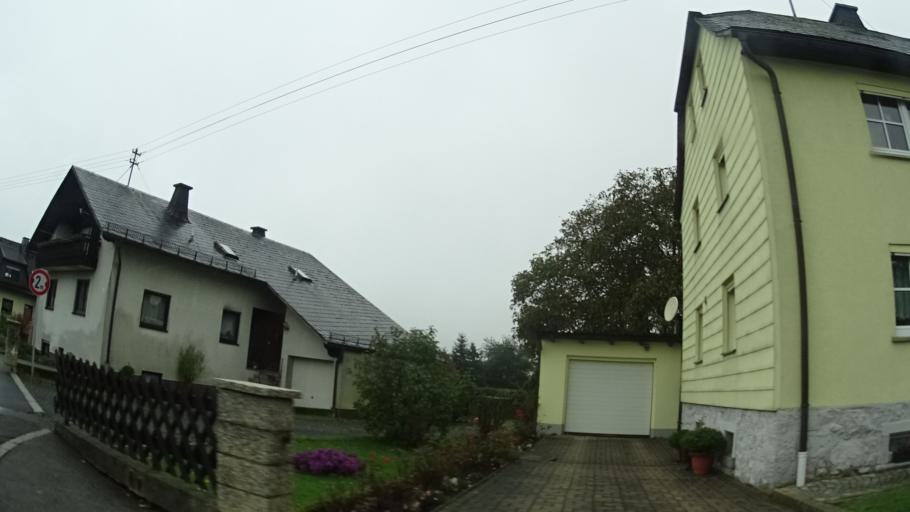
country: DE
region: Bavaria
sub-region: Upper Franconia
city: Wilhelmsthal
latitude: 50.3240
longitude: 11.3857
